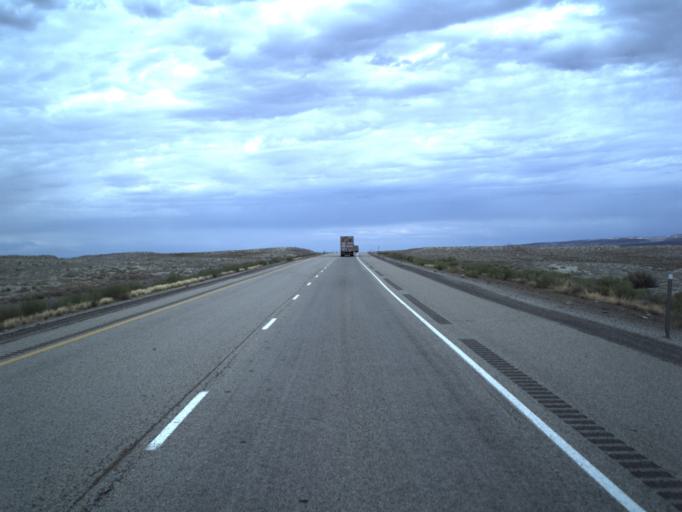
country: US
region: Utah
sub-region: Grand County
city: Moab
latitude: 38.9675
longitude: -109.3666
